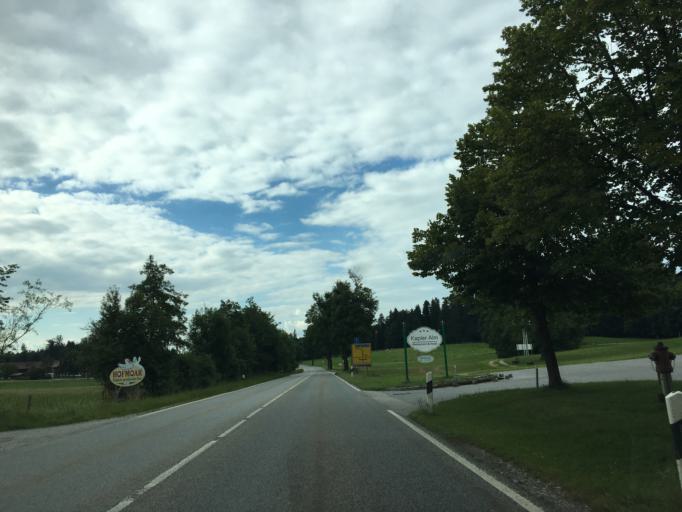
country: DE
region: Bavaria
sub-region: Upper Bavaria
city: Gmund am Tegernsee
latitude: 47.7873
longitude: 11.7230
